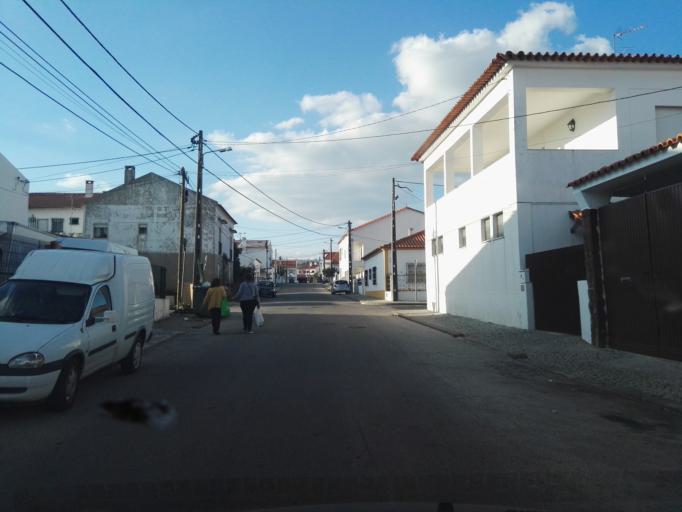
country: PT
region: Evora
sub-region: Evora
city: Evora
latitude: 38.5616
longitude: -7.9242
